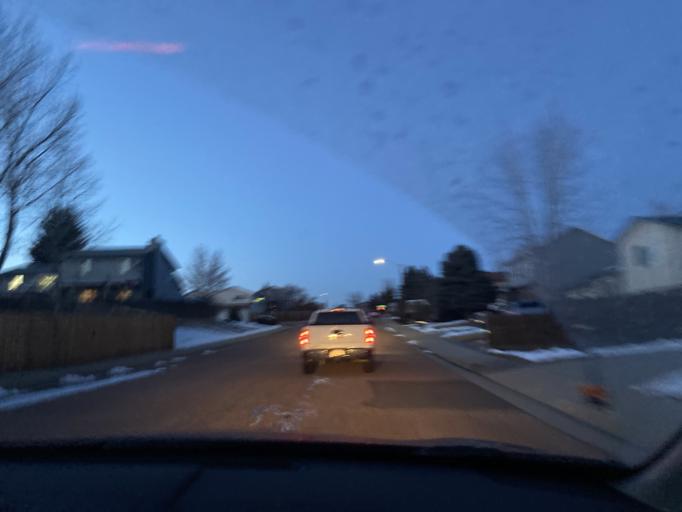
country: US
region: Colorado
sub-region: El Paso County
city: Security-Widefield
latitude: 38.7322
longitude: -104.6846
